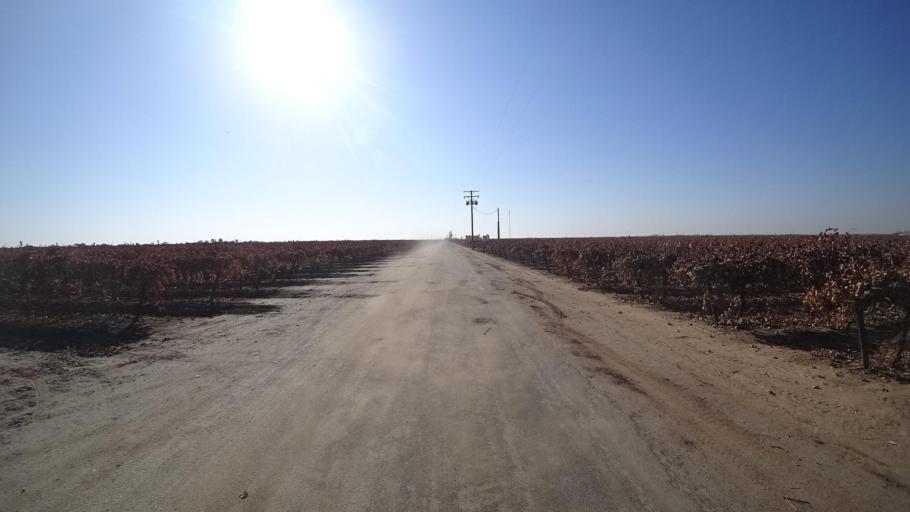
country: US
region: California
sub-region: Kern County
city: Delano
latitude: 35.7450
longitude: -119.2142
